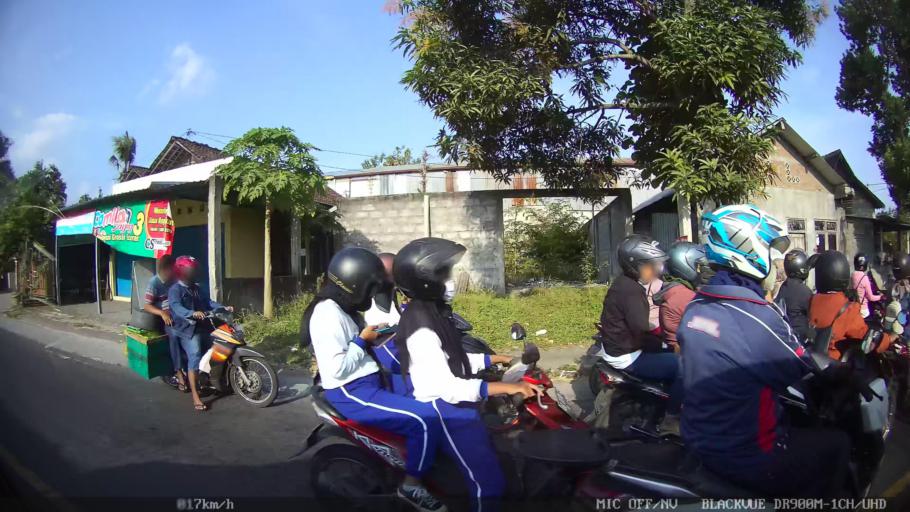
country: ID
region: Daerah Istimewa Yogyakarta
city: Bantul
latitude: -7.8786
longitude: 110.3197
